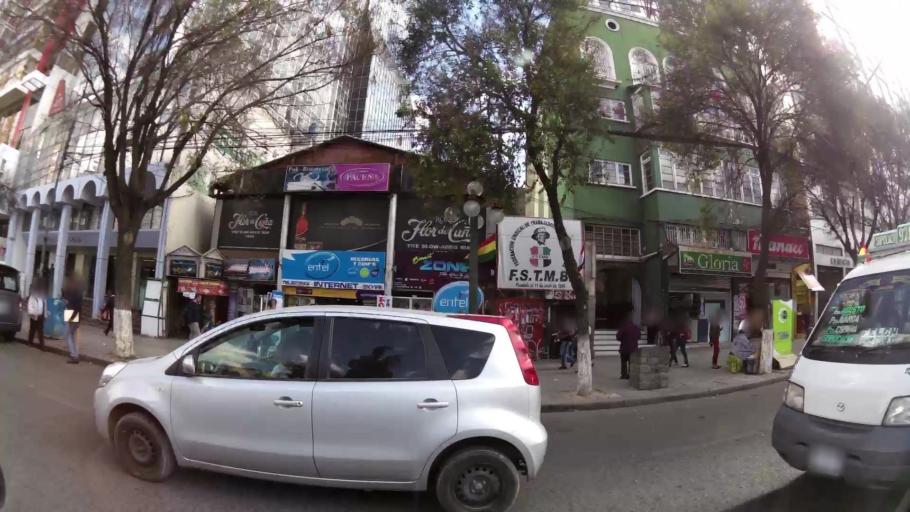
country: BO
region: La Paz
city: La Paz
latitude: -16.5010
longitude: -68.1334
